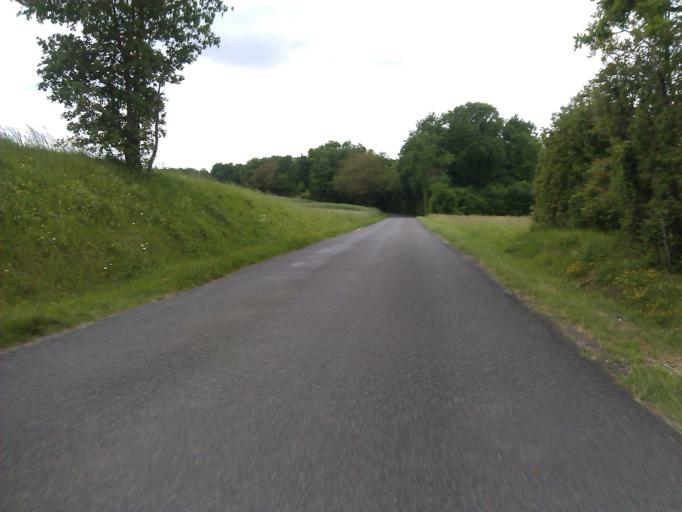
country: FR
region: Poitou-Charentes
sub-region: Departement de la Charente
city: Nersac
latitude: 45.6458
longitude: 0.0330
